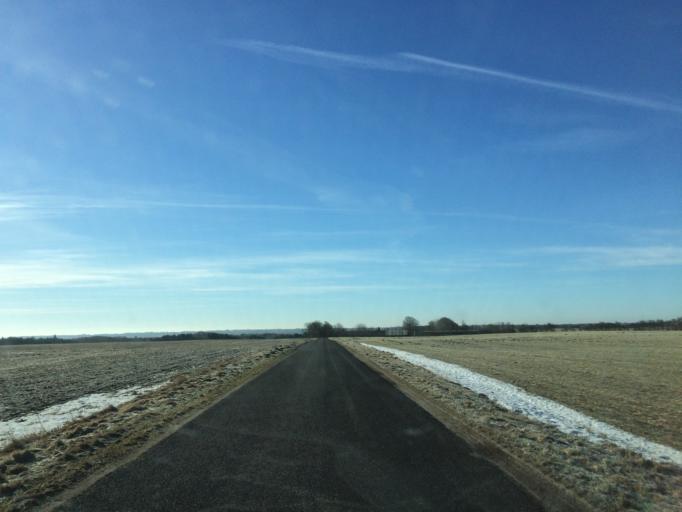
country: DK
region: North Denmark
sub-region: Mariagerfjord Kommune
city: Hobro
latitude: 56.6315
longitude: 9.6451
